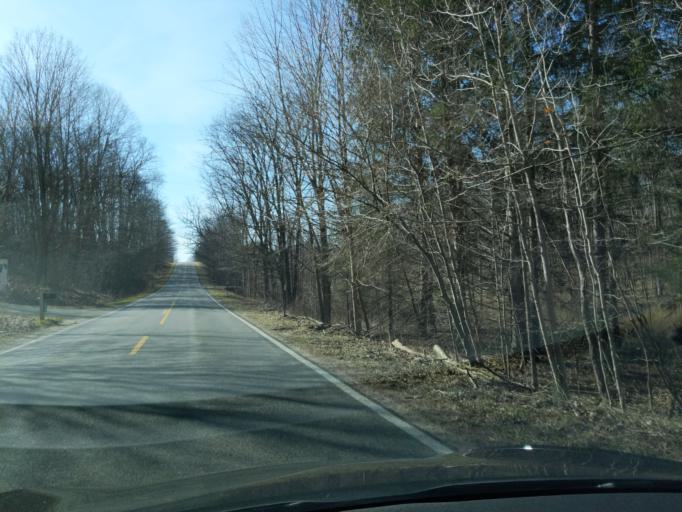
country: US
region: Michigan
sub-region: Ionia County
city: Saranac
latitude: 42.9296
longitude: -85.1587
